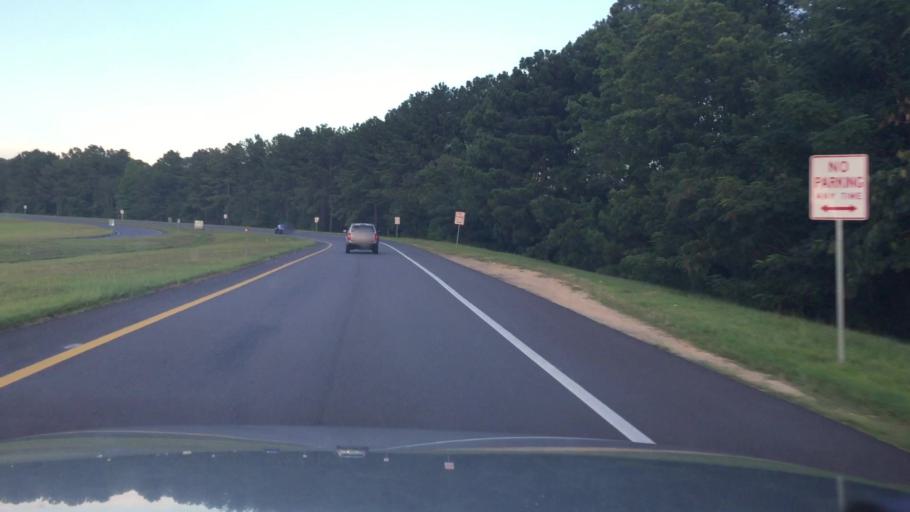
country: US
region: South Carolina
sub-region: Richland County
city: Forest Acres
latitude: 33.9489
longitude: -80.9735
